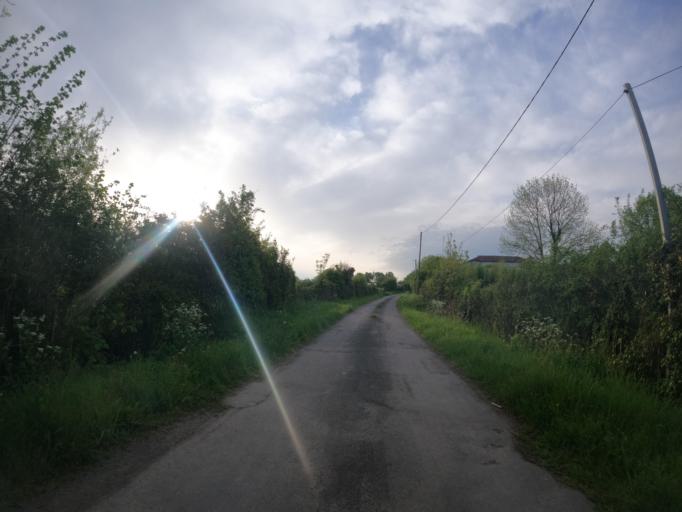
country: FR
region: Poitou-Charentes
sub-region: Departement des Deux-Sevres
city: Moncoutant
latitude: 46.7273
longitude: -0.5662
